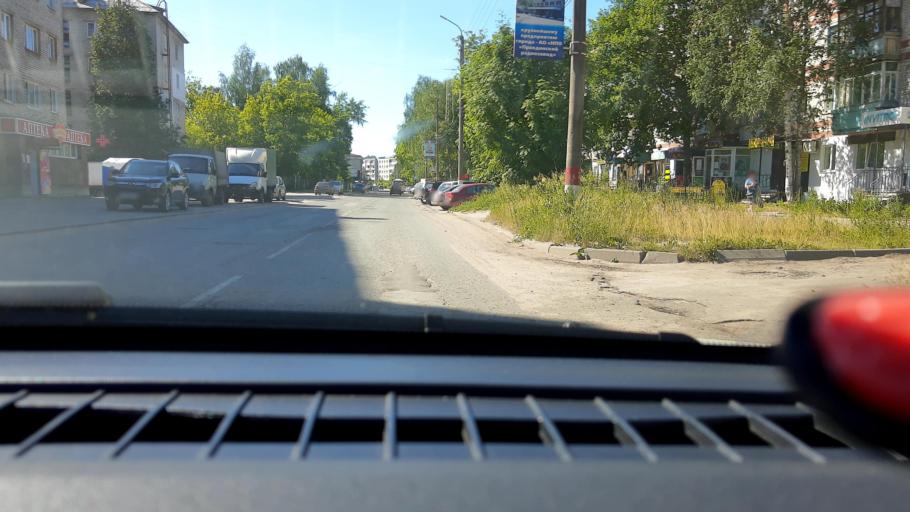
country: RU
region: Nizjnij Novgorod
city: Gidrotorf
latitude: 56.5191
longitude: 43.5529
